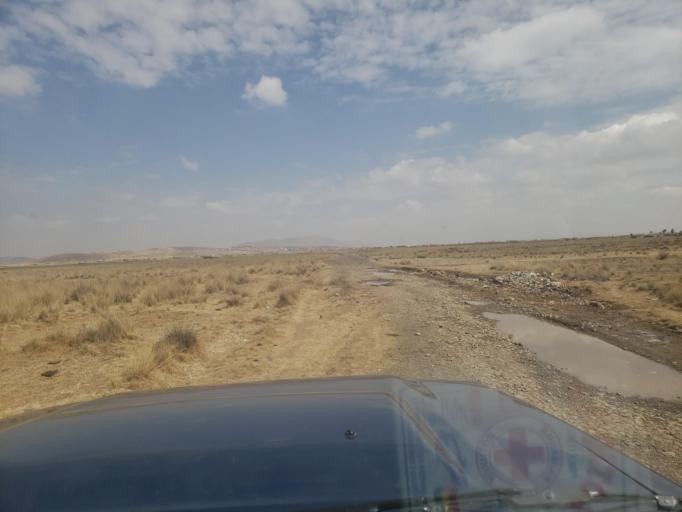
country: BO
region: La Paz
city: Batallas
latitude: -16.4106
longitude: -68.4404
